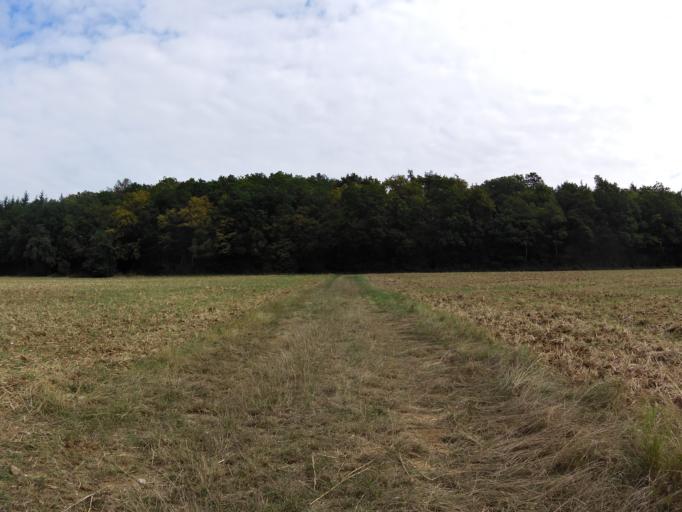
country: DE
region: Bavaria
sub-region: Regierungsbezirk Unterfranken
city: Kleinrinderfeld
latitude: 49.7129
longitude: 9.8332
